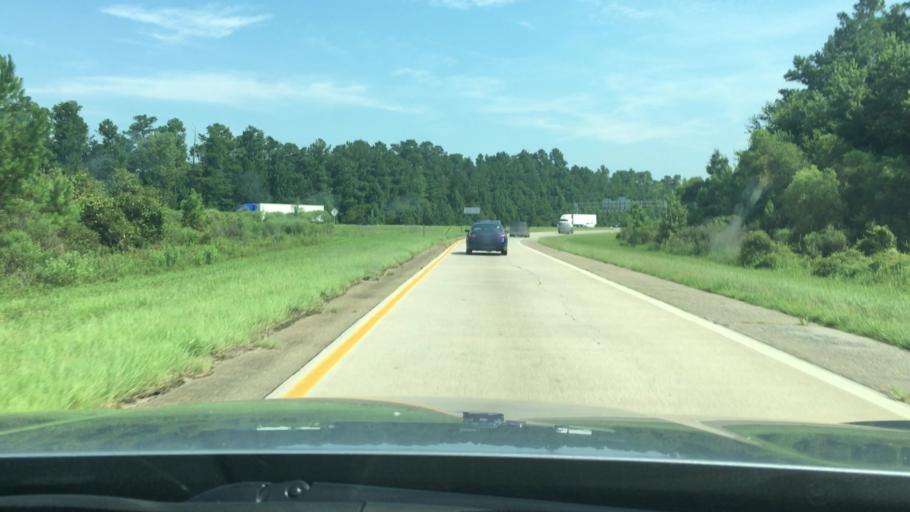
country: US
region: South Carolina
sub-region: Orangeburg County
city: Holly Hill
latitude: 33.3208
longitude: -80.5451
